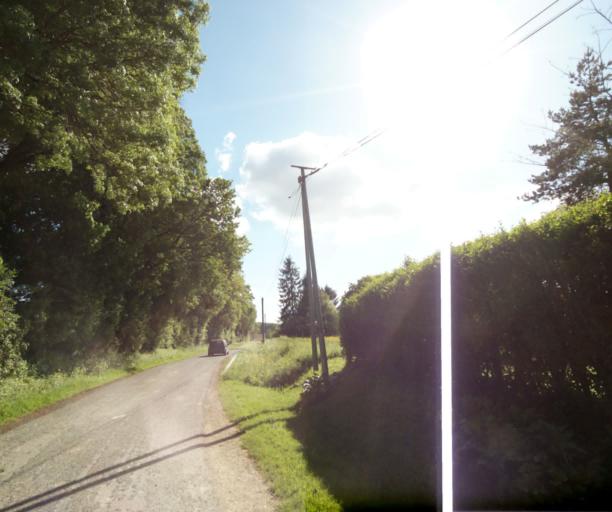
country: FR
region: Poitou-Charentes
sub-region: Departement de la Charente-Maritime
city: Chermignac
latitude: 45.7236
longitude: -0.6922
